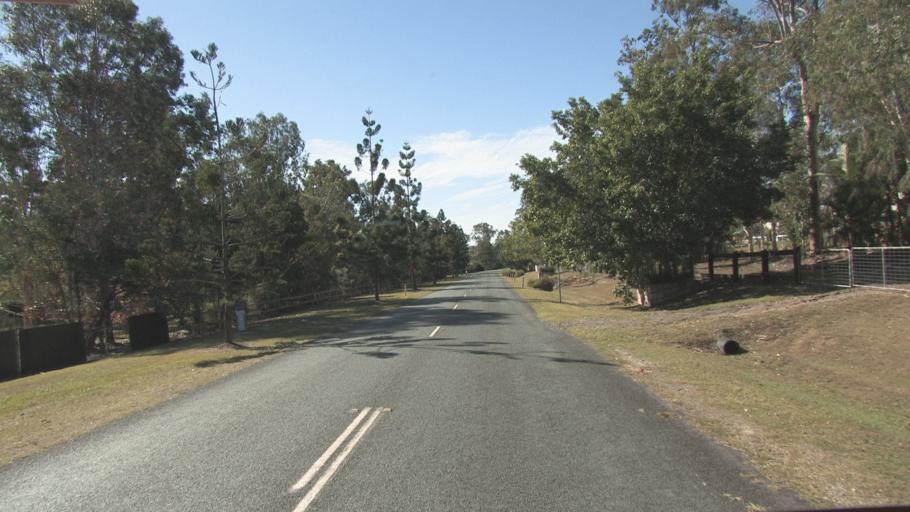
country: AU
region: Queensland
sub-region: Ipswich
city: Springfield Lakes
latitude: -27.7328
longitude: 152.9238
